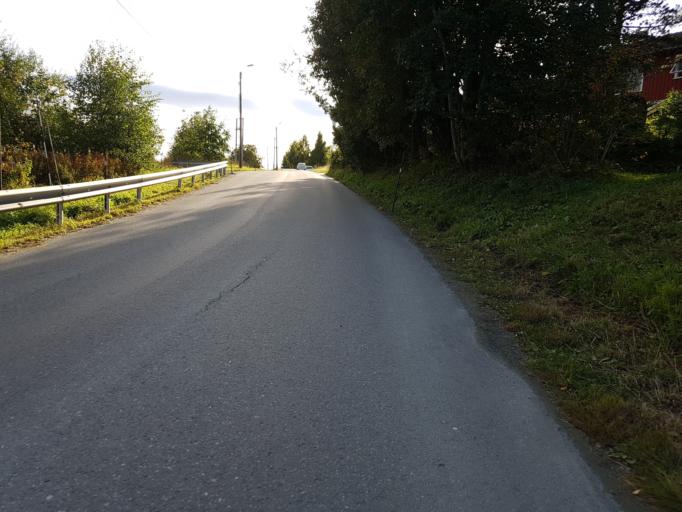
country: NO
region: Sor-Trondelag
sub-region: Klaebu
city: Klaebu
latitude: 63.3496
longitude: 10.4865
